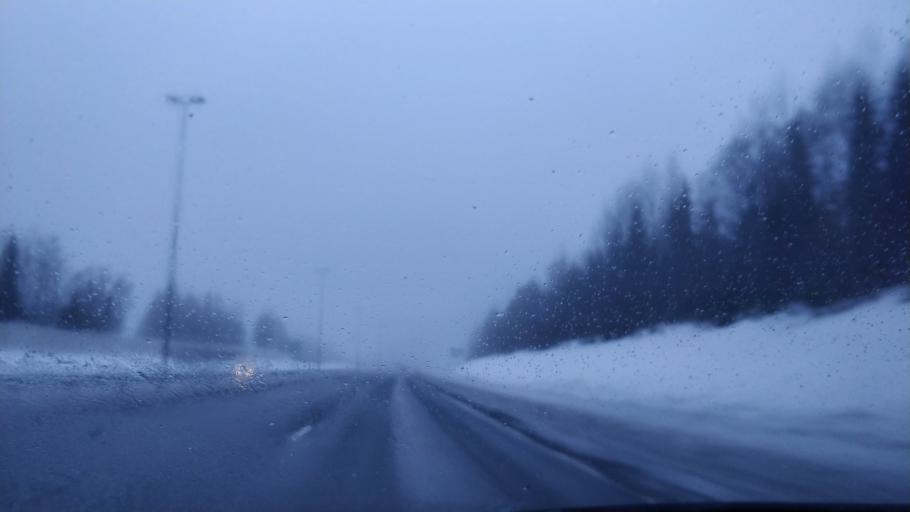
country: FI
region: Lapland
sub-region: Kemi-Tornio
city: Kemi
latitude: 65.7512
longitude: 24.5751
